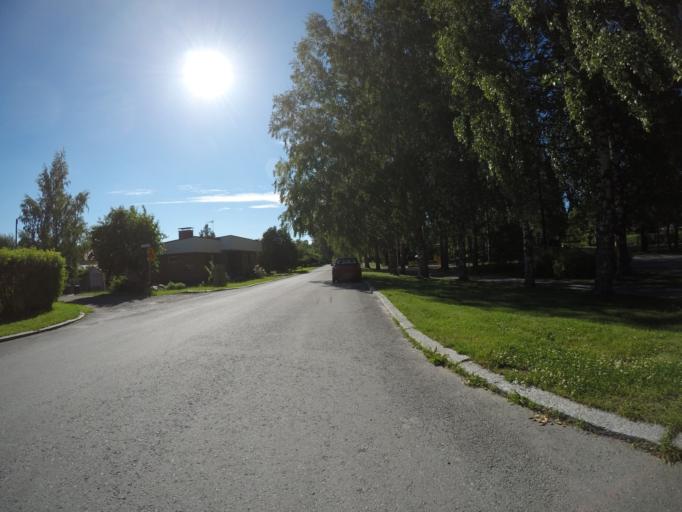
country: FI
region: Haeme
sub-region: Haemeenlinna
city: Haemeenlinna
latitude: 61.0038
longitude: 24.4791
